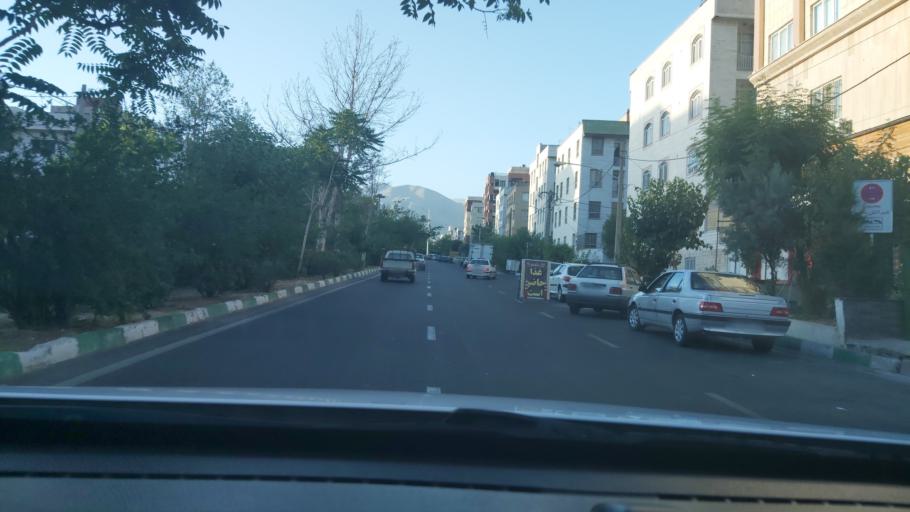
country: IR
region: Tehran
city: Tehran
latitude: 35.7296
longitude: 51.3047
